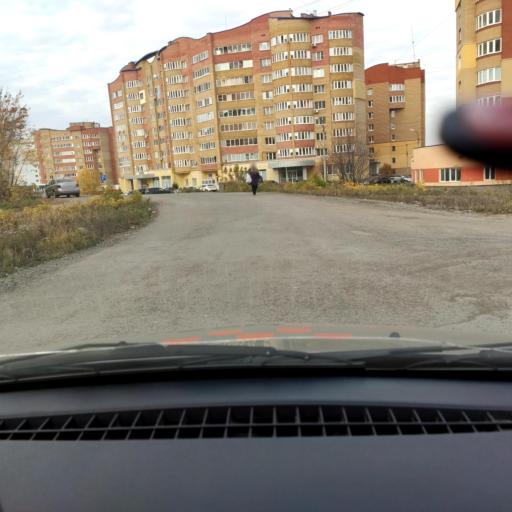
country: RU
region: Bashkortostan
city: Ufa
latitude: 54.7043
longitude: 55.9851
